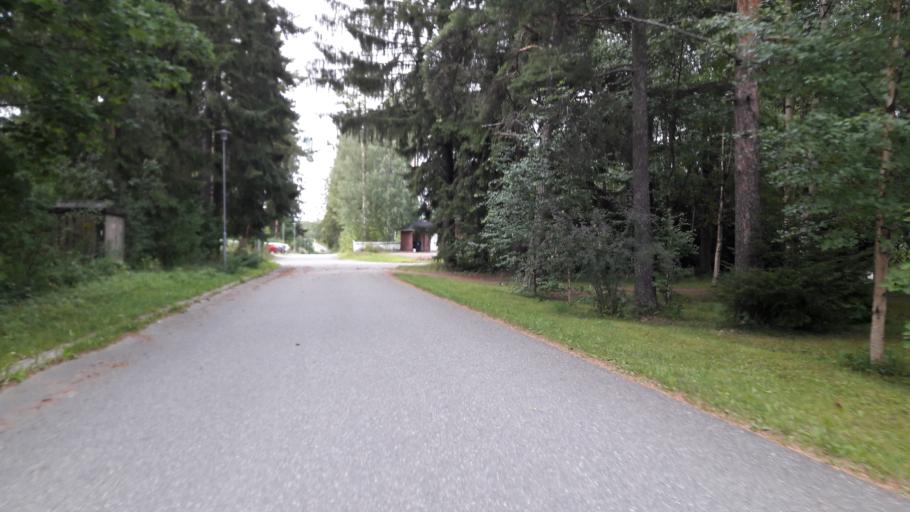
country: FI
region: North Karelia
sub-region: Joensuu
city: Joensuu
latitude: 62.5804
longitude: 29.7669
